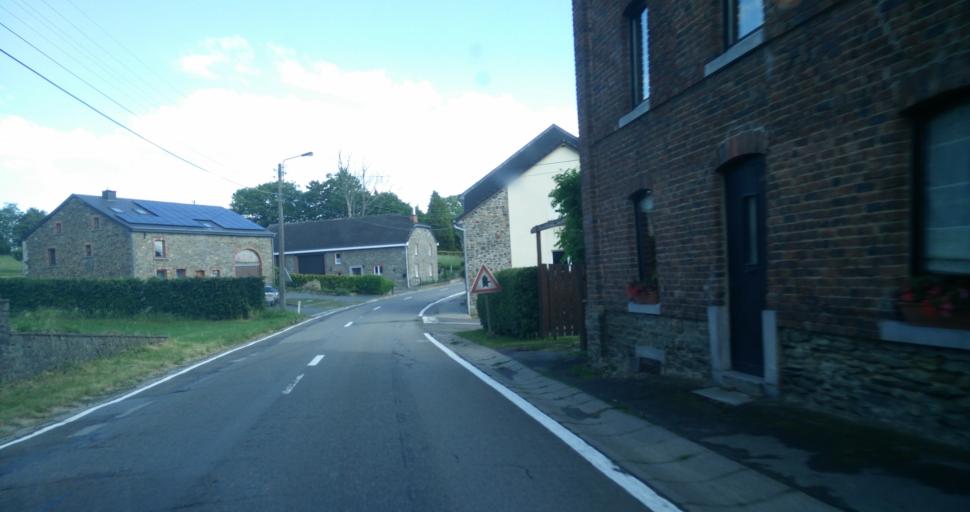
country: BE
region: Wallonia
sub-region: Province du Luxembourg
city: La Roche-en-Ardenne
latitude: 50.1772
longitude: 5.6656
